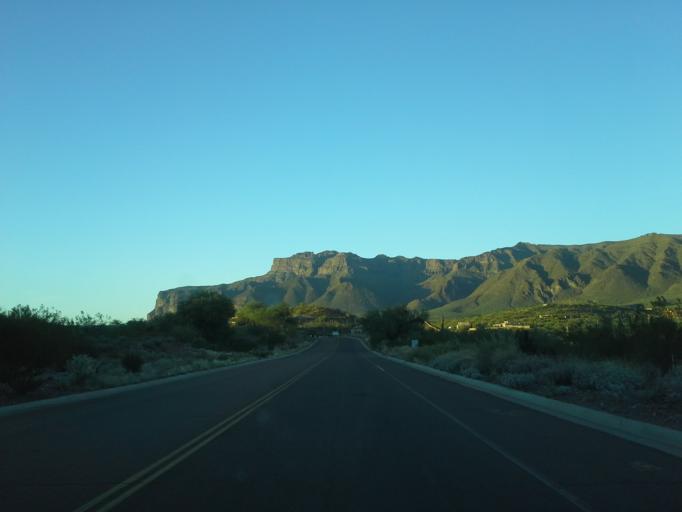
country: US
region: Arizona
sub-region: Pinal County
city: Apache Junction
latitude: 33.3765
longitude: -111.4431
